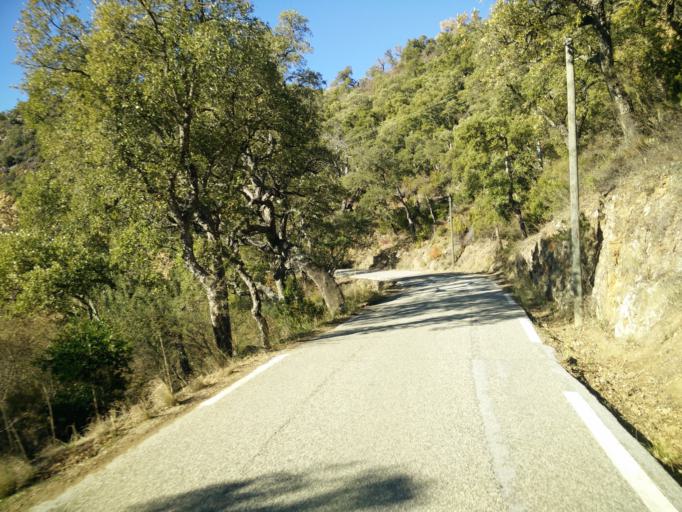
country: FR
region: Provence-Alpes-Cote d'Azur
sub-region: Departement du Var
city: La Garde-Freinet
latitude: 43.2577
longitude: 6.4437
